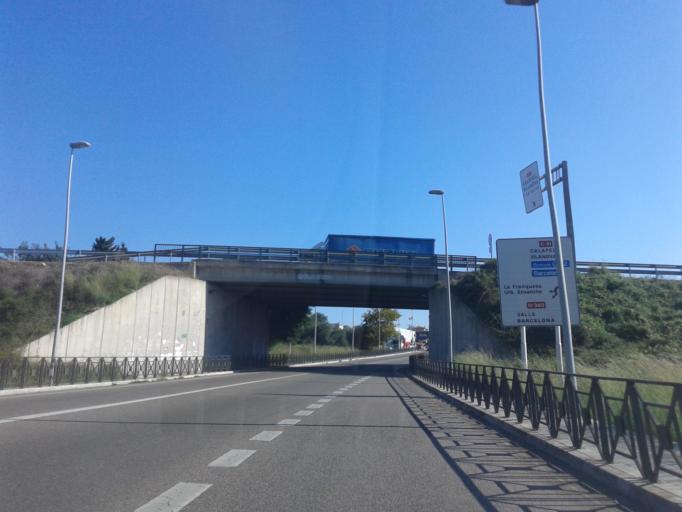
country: ES
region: Catalonia
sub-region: Provincia de Tarragona
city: El Vendrell
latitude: 41.2185
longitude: 1.5445
